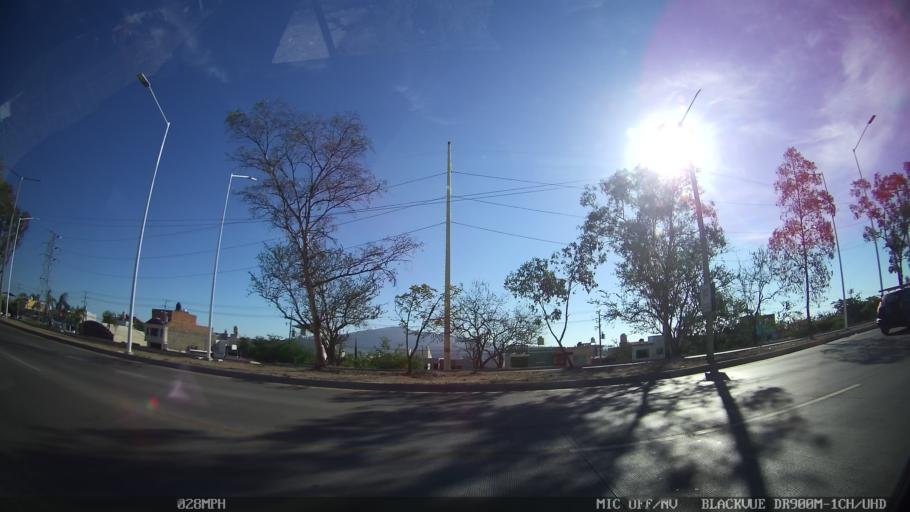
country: MX
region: Jalisco
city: Tlaquepaque
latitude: 20.7009
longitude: -103.2793
